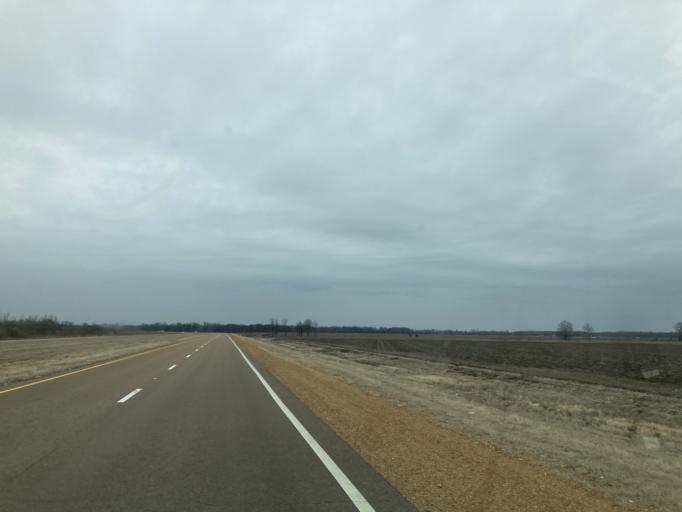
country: US
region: Mississippi
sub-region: Humphreys County
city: Belzoni
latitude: 33.0642
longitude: -90.4719
